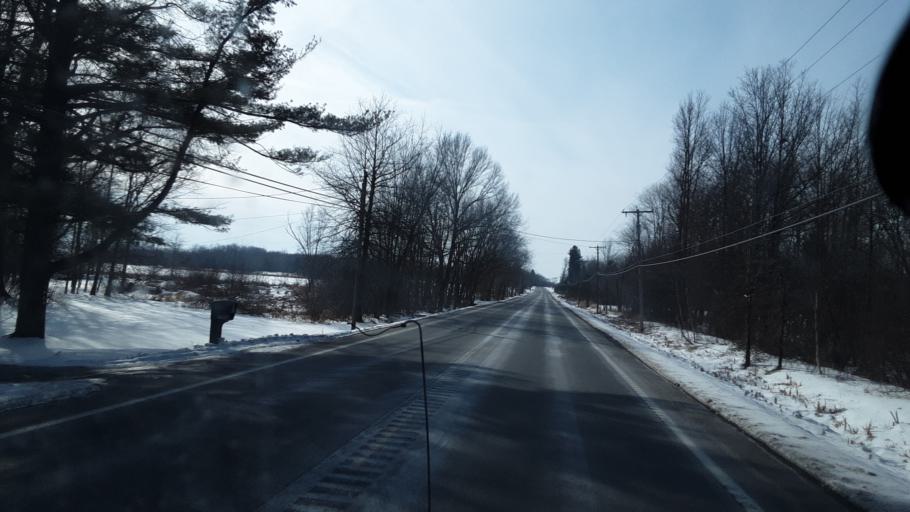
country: US
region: Ohio
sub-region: Stark County
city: Alliance
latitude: 41.0245
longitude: -81.1026
